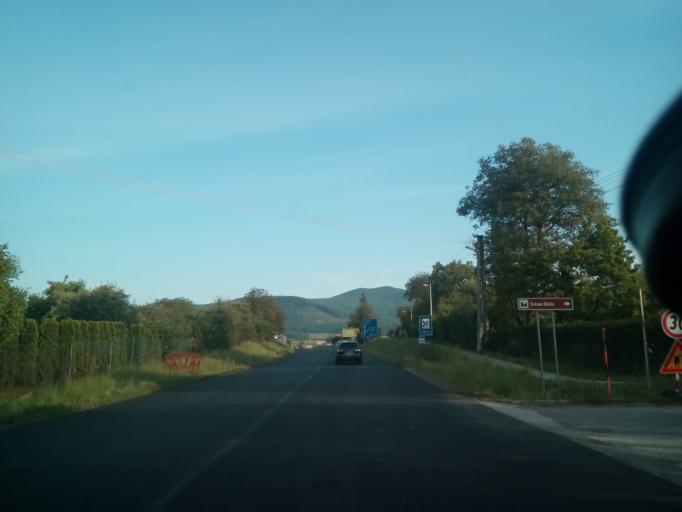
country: SK
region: Kosicky
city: Roznava
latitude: 48.6469
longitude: 20.6015
